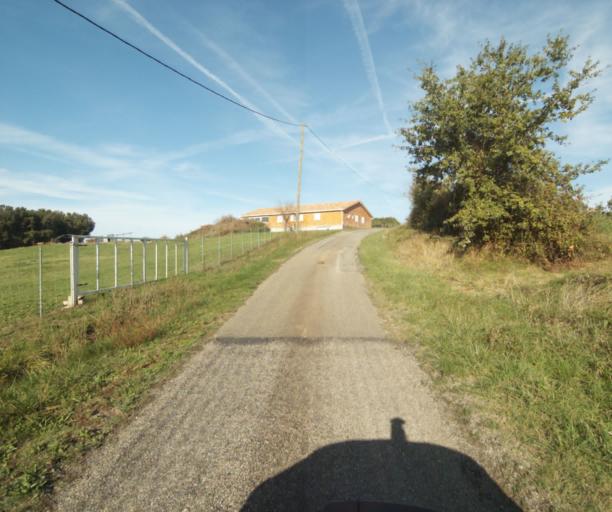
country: FR
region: Midi-Pyrenees
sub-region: Departement du Tarn-et-Garonne
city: Finhan
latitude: 43.9186
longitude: 1.1238
